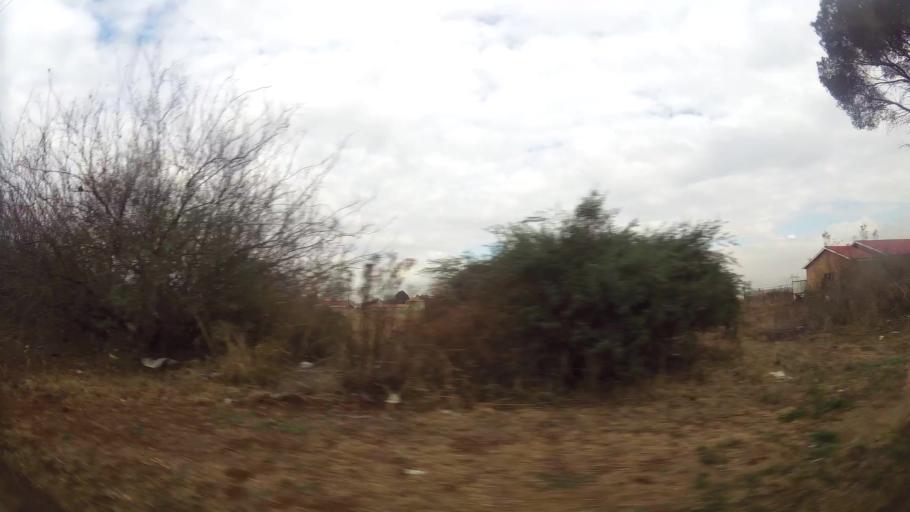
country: ZA
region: Gauteng
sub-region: Sedibeng District Municipality
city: Meyerton
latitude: -26.5918
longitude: 27.9933
